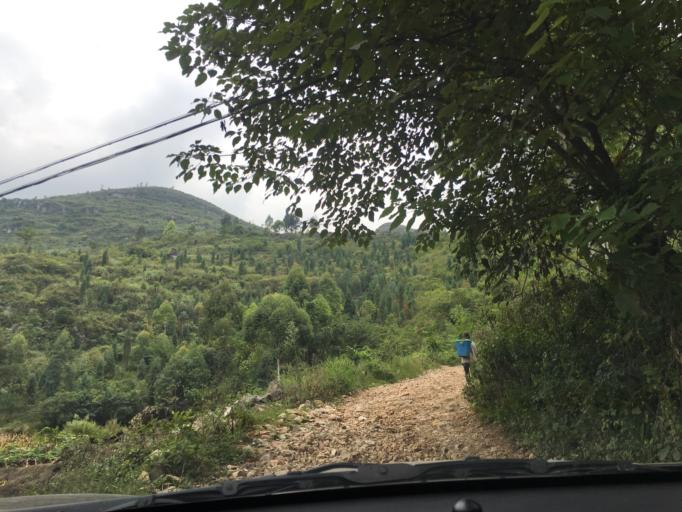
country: CN
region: Guangxi Zhuangzu Zizhiqu
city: Xinzhou
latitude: 25.3796
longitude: 105.6379
